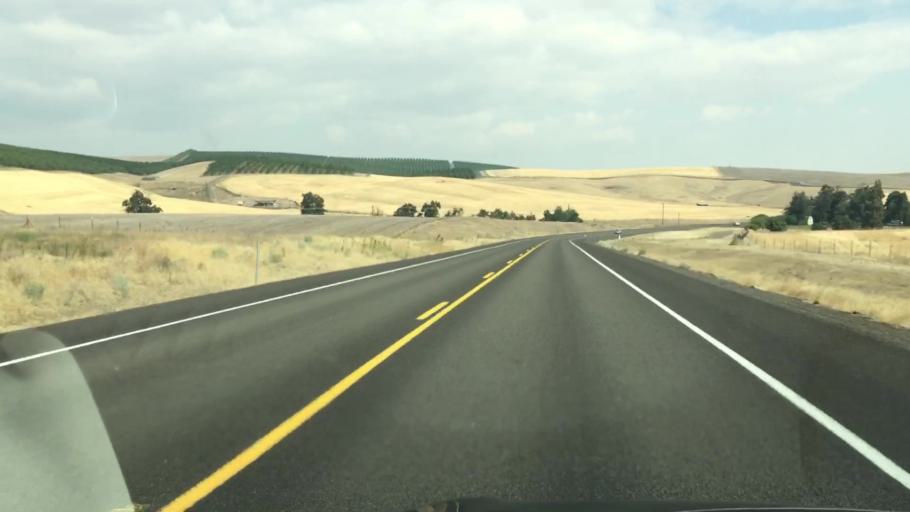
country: US
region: Oregon
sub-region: Wasco County
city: The Dalles
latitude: 45.4807
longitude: -121.1167
